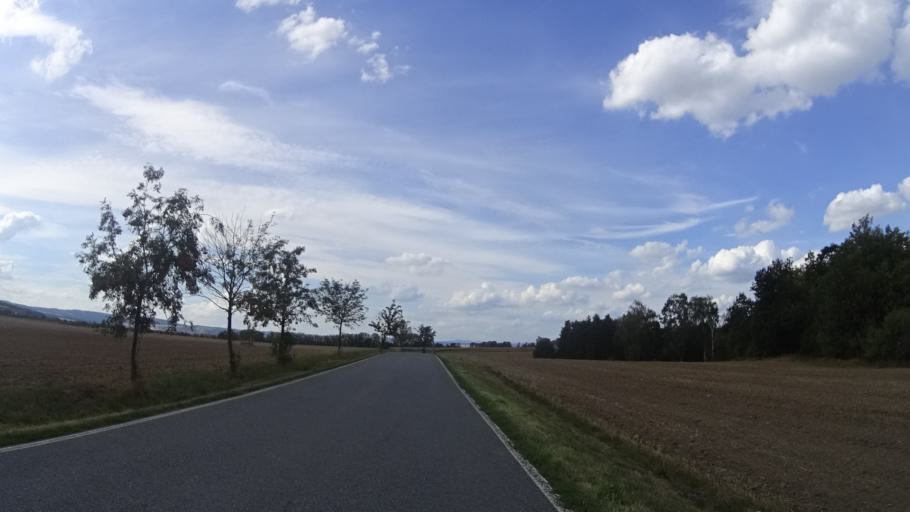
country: CZ
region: Olomoucky
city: Bila Lhota
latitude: 49.7336
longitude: 16.9777
